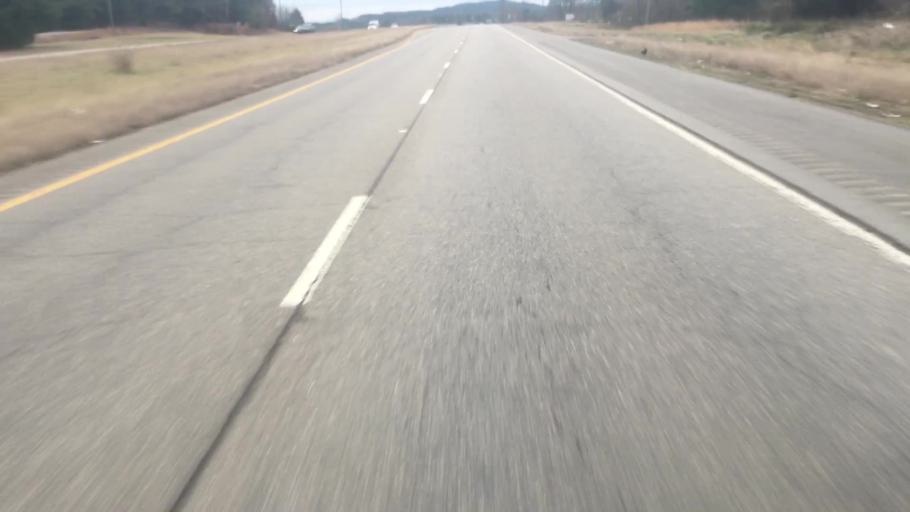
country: US
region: Alabama
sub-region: Walker County
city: Dora
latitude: 33.7982
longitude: -87.1129
